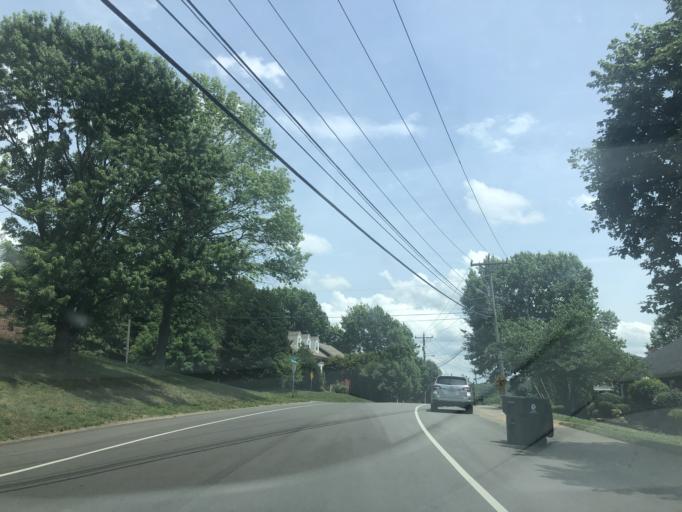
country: US
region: Tennessee
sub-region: Cheatham County
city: Pegram
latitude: 36.0525
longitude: -86.9591
